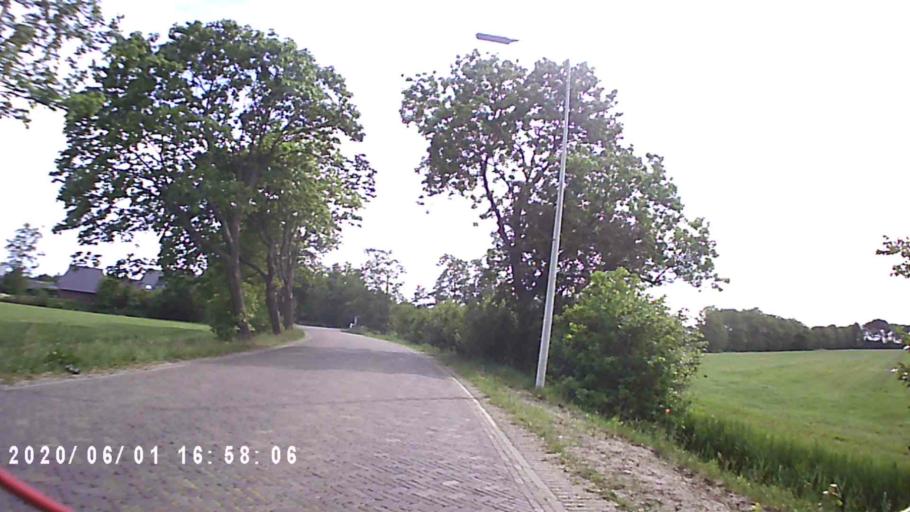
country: NL
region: Friesland
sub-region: Gemeente Tytsjerksteradiel
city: Hurdegaryp
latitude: 53.1905
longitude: 5.9278
